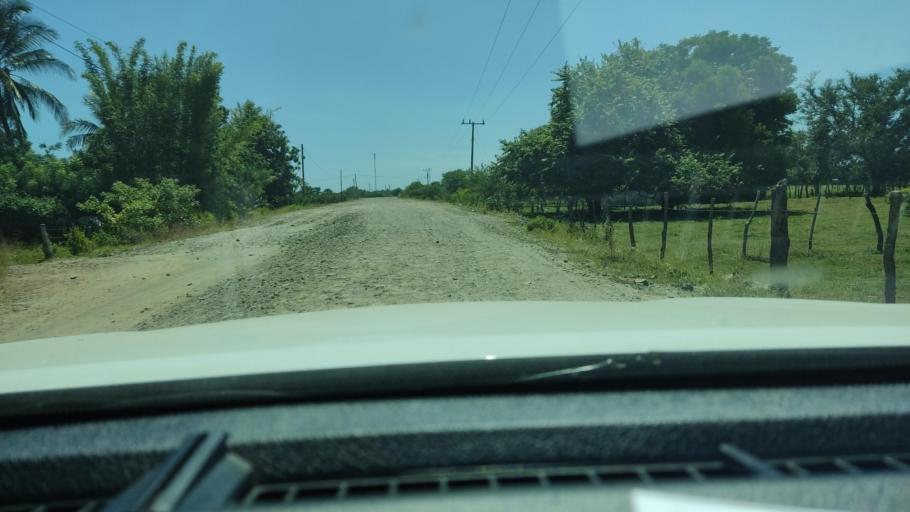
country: SV
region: Ahuachapan
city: San Francisco Menendez
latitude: 13.7651
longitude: -90.1688
